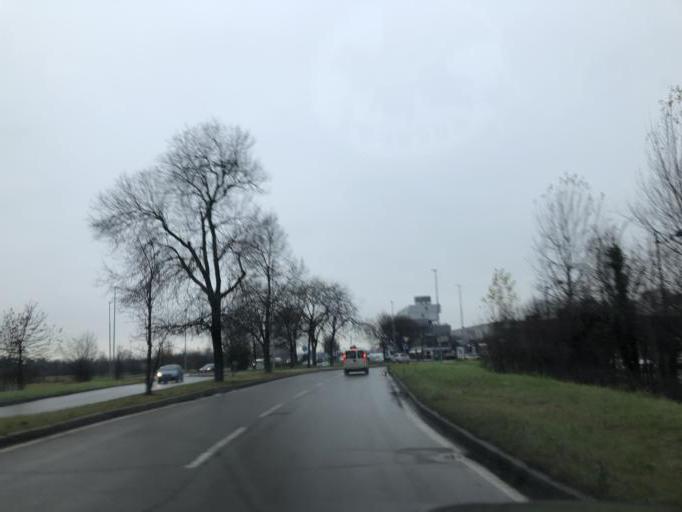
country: IT
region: Emilia-Romagna
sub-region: Provincia di Modena
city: Modena
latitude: 44.6377
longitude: 10.8889
